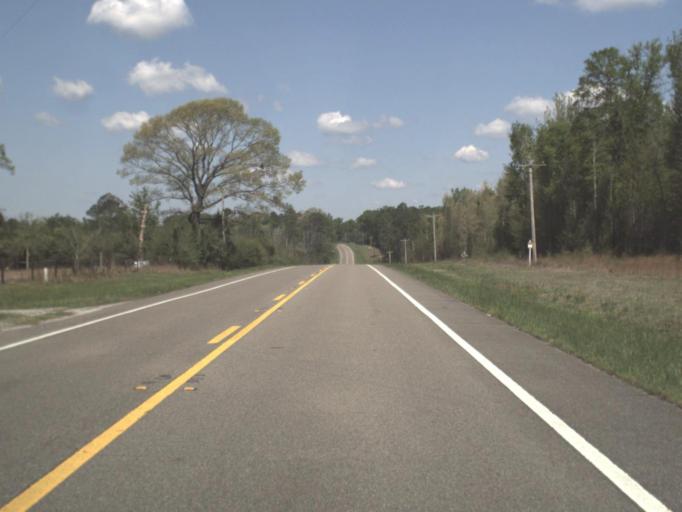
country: US
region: Alabama
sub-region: Escambia County
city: East Brewton
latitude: 30.9394
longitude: -87.0649
